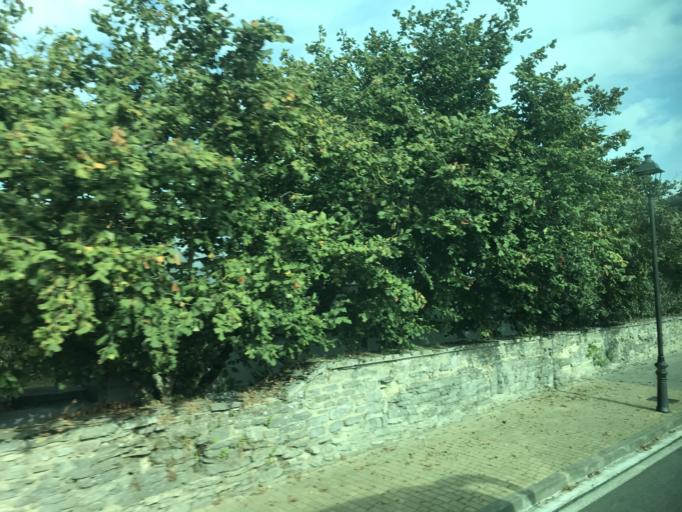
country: ES
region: Basque Country
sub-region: Provincia de Alava
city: Gasteiz / Vitoria
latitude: 42.9344
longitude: -2.6421
